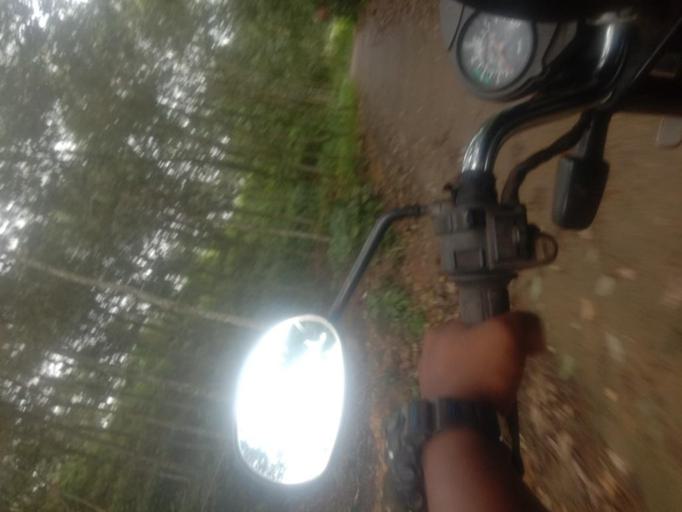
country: IN
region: Kerala
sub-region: Thiruvananthapuram
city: Nedumangad
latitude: 8.6999
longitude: 76.9581
